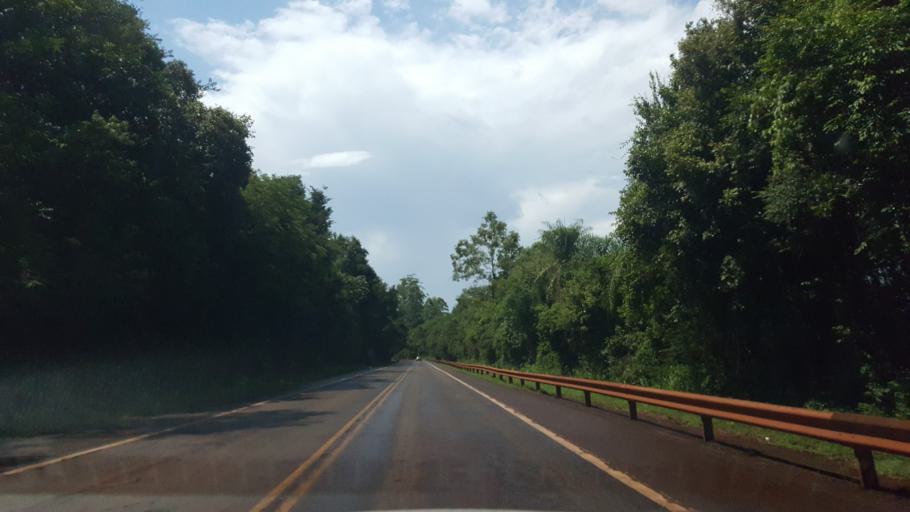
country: AR
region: Misiones
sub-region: Departamento de Eldorado
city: Eldorado
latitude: -26.3565
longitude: -54.6179
